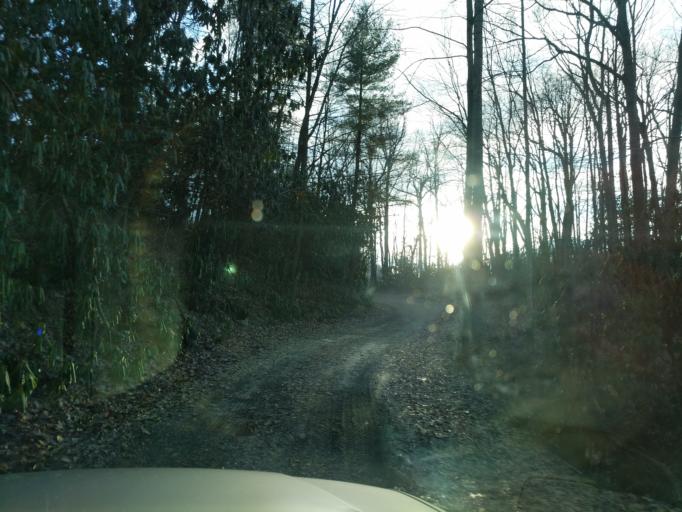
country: US
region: North Carolina
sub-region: Haywood County
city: Cove Creek
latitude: 35.7332
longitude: -83.0545
